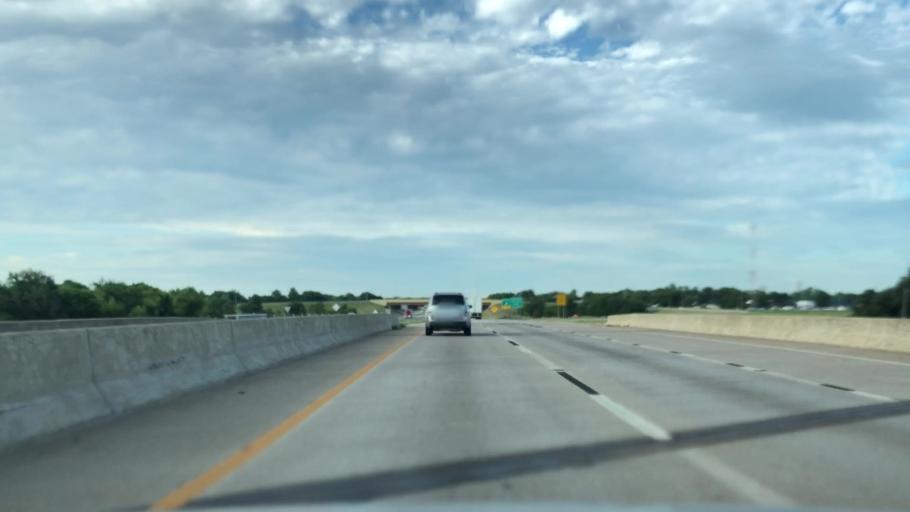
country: US
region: Oklahoma
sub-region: Tulsa County
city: Turley
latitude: 36.2106
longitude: -95.9457
